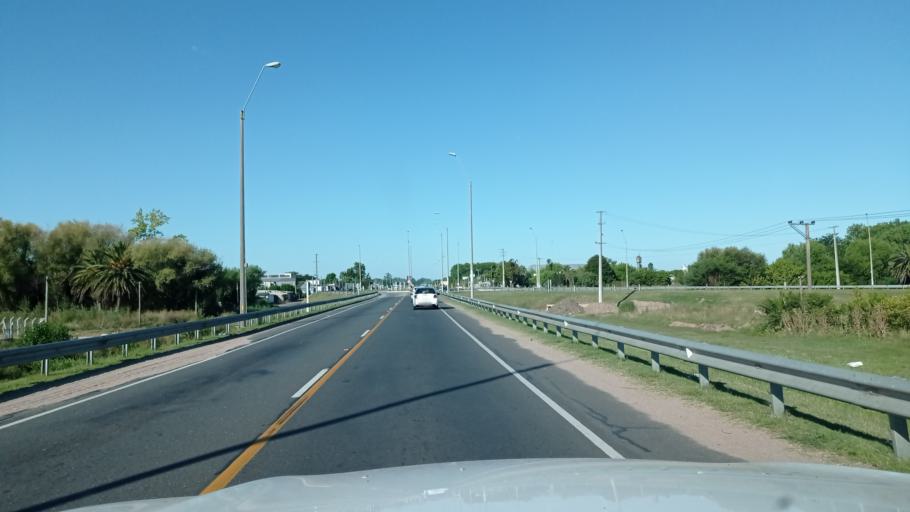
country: UY
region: Canelones
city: Pando
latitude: -34.7184
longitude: -55.9509
